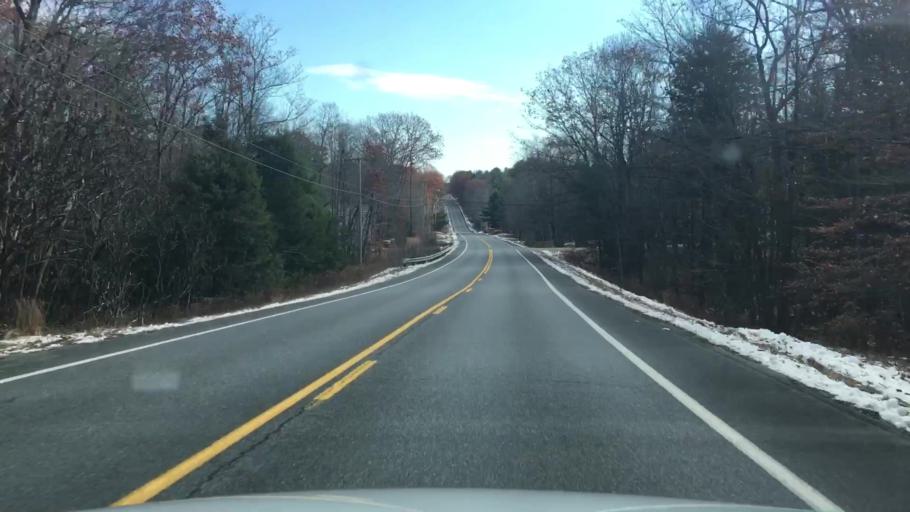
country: US
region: Maine
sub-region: Kennebec County
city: Winthrop
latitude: 44.3264
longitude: -69.9922
